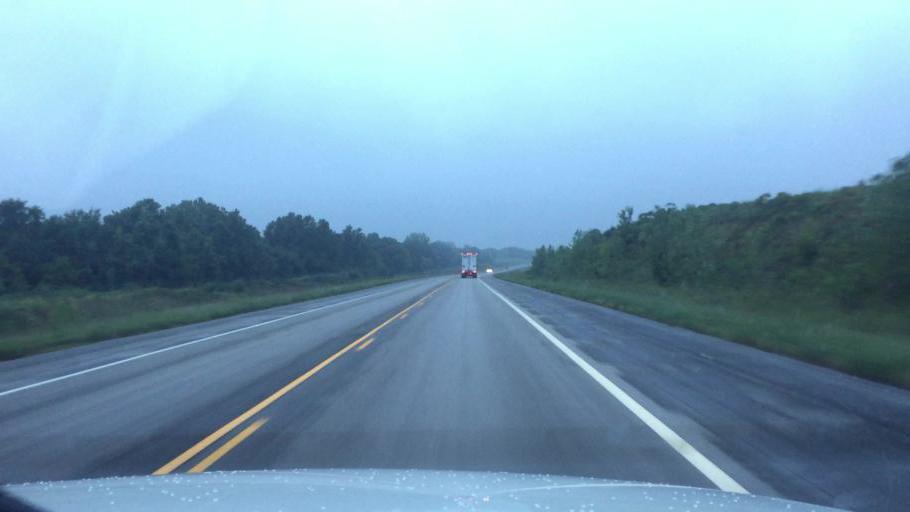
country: US
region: Kansas
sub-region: Montgomery County
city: Cherryvale
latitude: 37.4497
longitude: -95.4833
